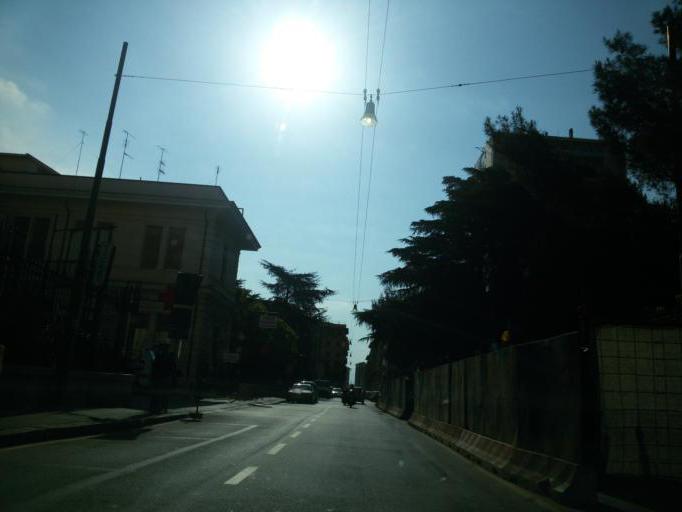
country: IT
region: Liguria
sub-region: Provincia di Genova
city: San Teodoro
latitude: 44.4127
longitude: 8.8963
